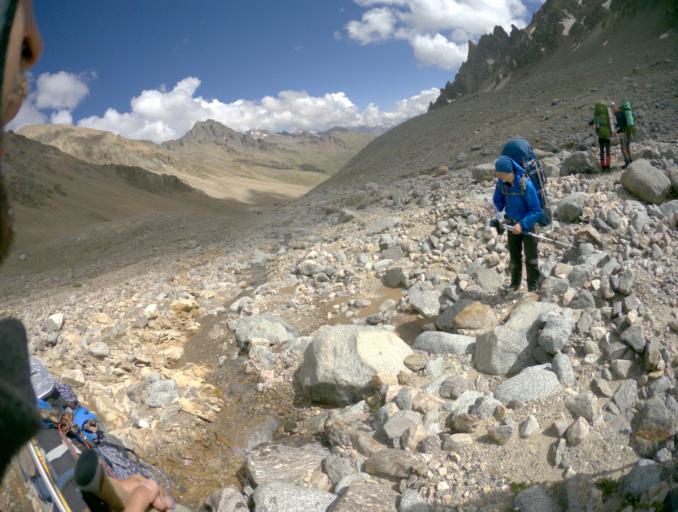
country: RU
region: Kabardino-Balkariya
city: Terskol
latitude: 43.3347
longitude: 42.5506
